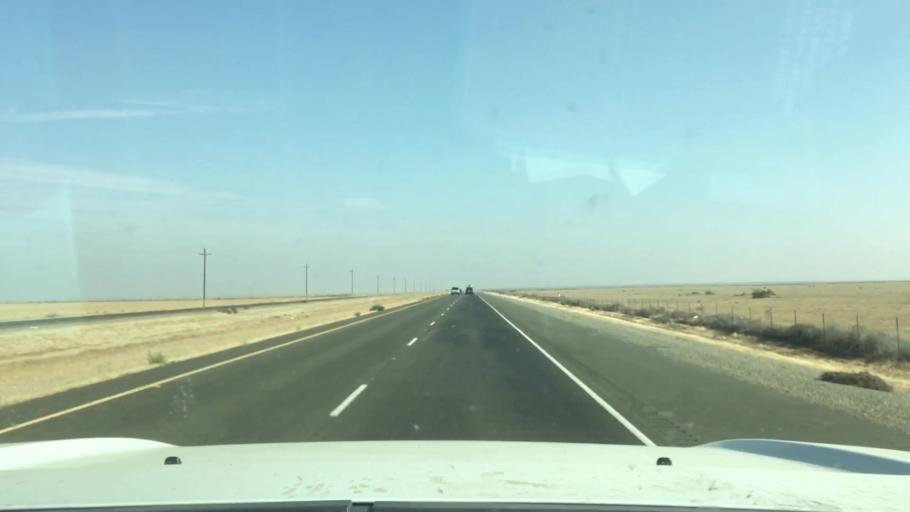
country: US
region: California
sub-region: Kern County
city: Lost Hills
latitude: 35.6156
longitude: -119.7941
